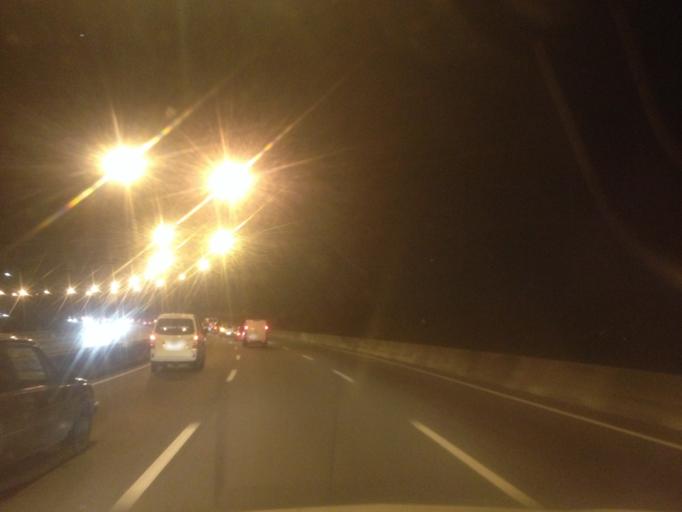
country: BR
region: Rio de Janeiro
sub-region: Duque De Caxias
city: Duque de Caxias
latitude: -22.8235
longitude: -43.2518
